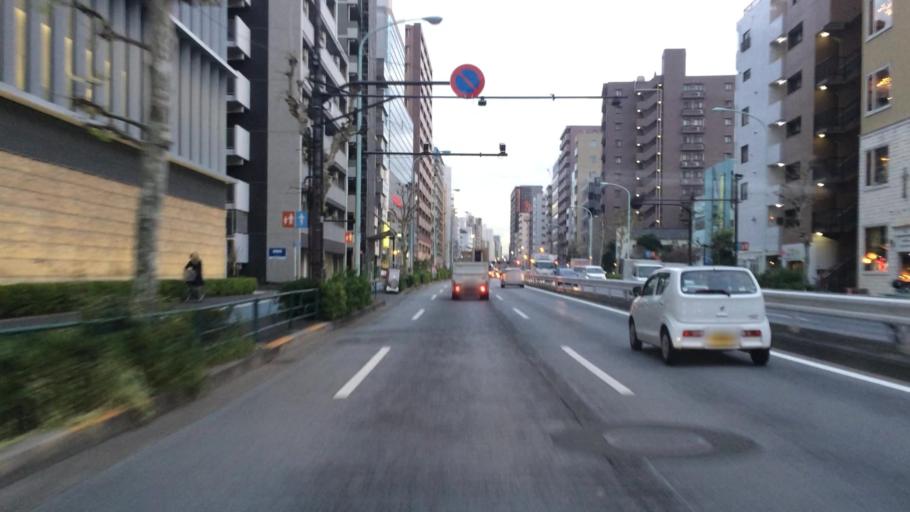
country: JP
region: Tokyo
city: Tokyo
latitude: 35.6397
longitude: 139.7032
